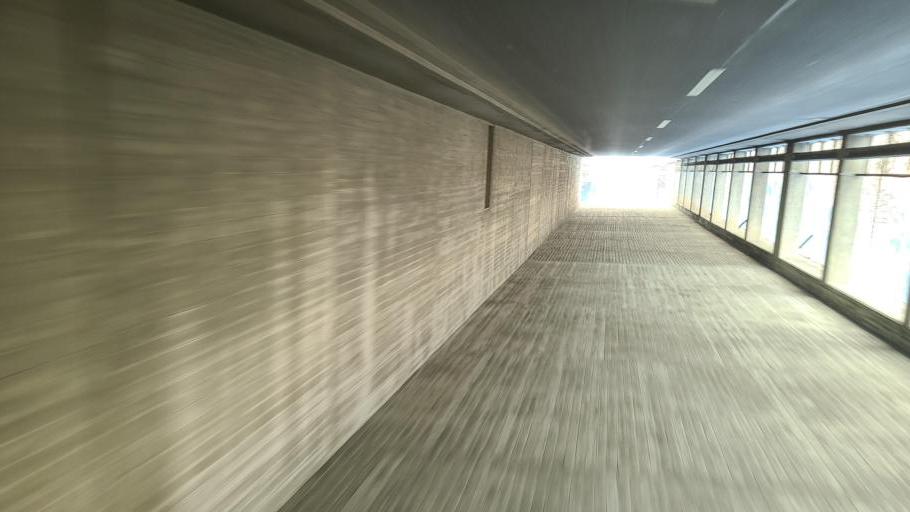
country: CH
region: Grisons
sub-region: Inn District
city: Zernez
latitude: 46.7379
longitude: 10.0793
